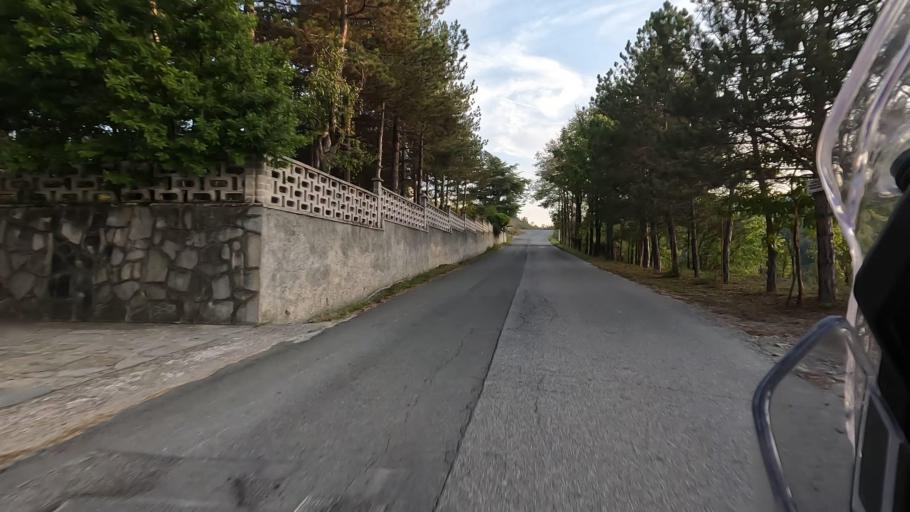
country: IT
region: Liguria
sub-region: Provincia di Savona
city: Mioglia
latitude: 44.4791
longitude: 8.4141
